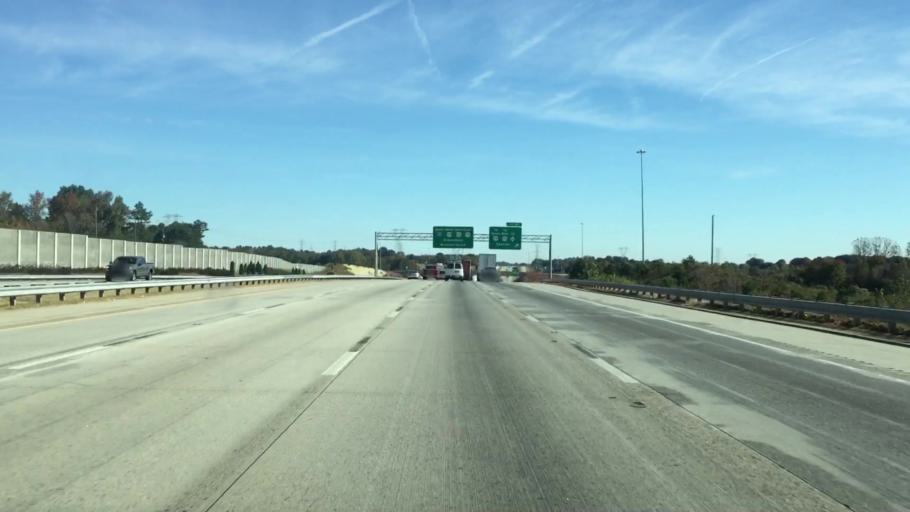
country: US
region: North Carolina
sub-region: Rowan County
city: Spencer
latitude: 35.7279
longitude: -80.3811
